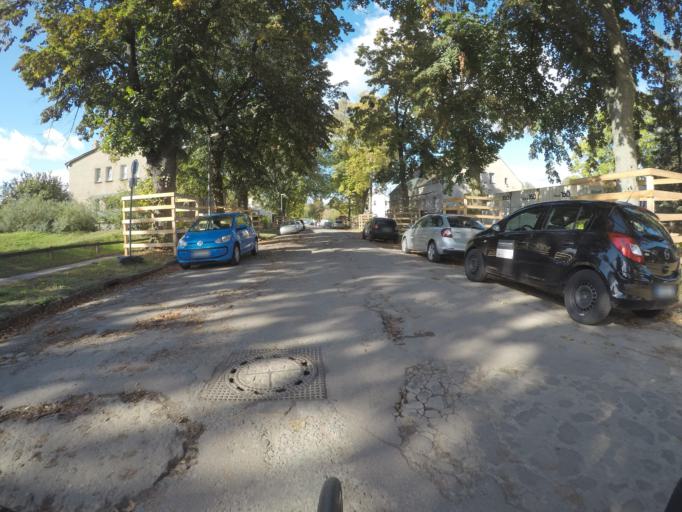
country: DE
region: Berlin
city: Staaken
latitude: 52.5307
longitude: 13.1390
